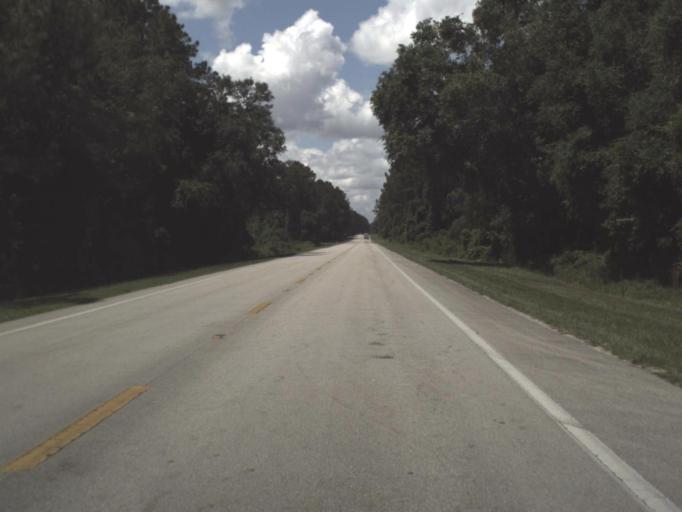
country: US
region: Florida
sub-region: Putnam County
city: Crescent City
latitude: 29.3958
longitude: -81.5090
